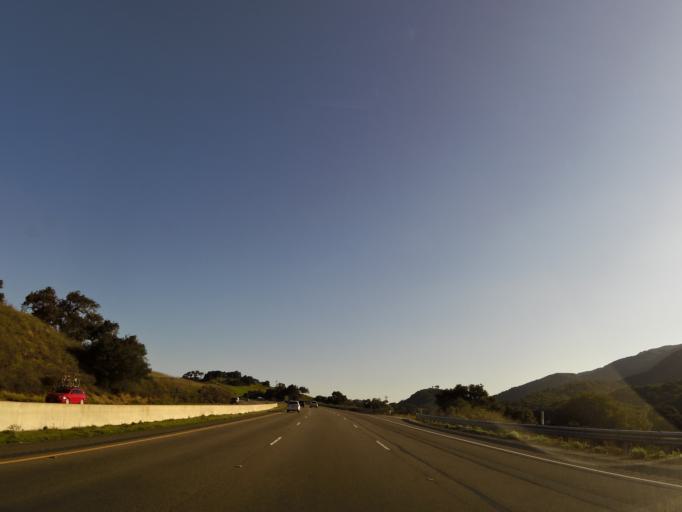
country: US
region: California
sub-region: Santa Barbara County
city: Buellton
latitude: 34.5238
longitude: -120.2027
